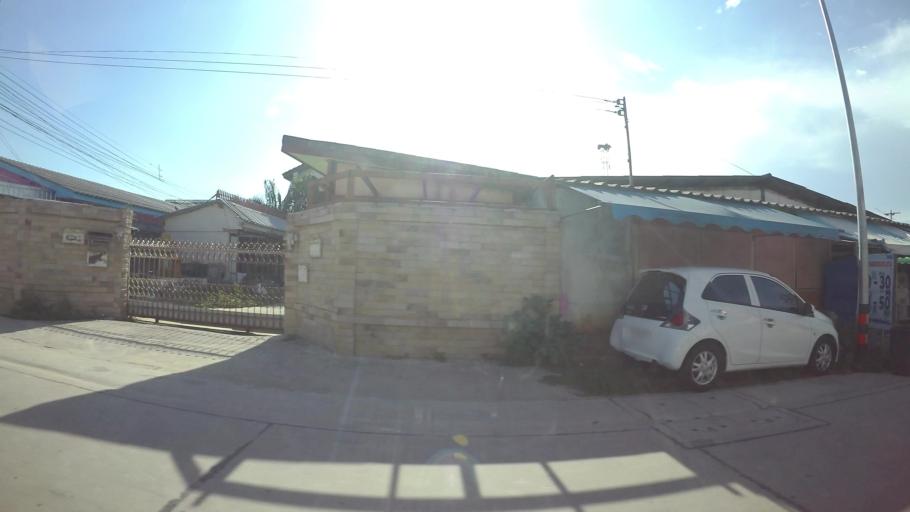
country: TH
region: Rayong
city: Rayong
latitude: 12.6685
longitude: 101.2991
